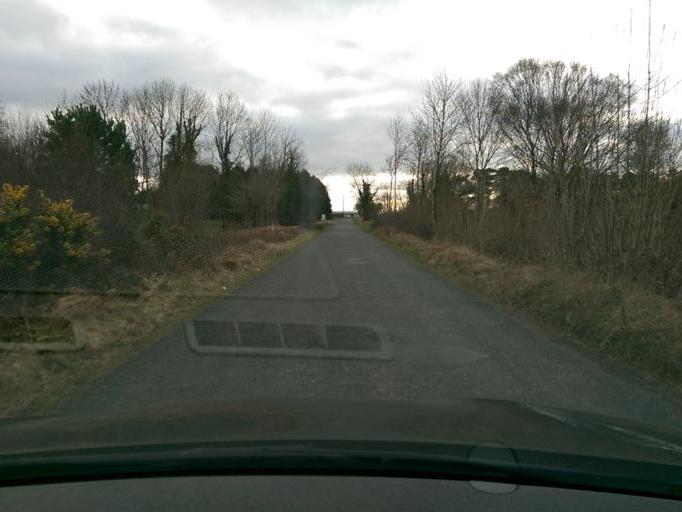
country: IE
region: Leinster
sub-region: Uibh Fhaili
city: Ferbane
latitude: 53.3277
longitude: -7.8797
